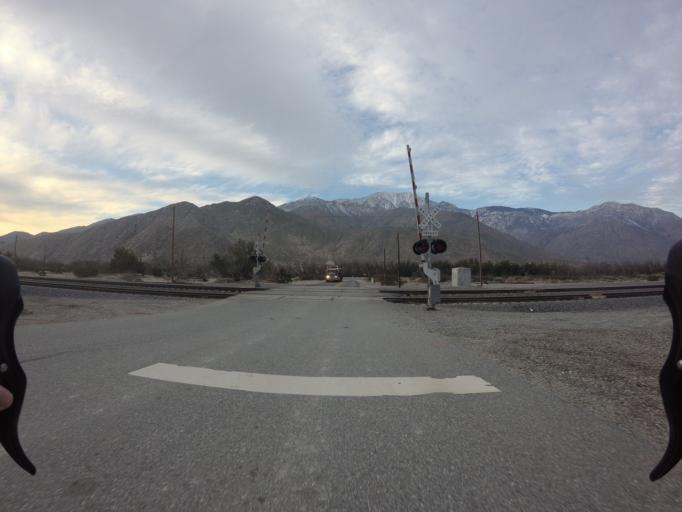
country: US
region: California
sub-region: Riverside County
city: Garnet
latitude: 33.9044
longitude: -116.6428
